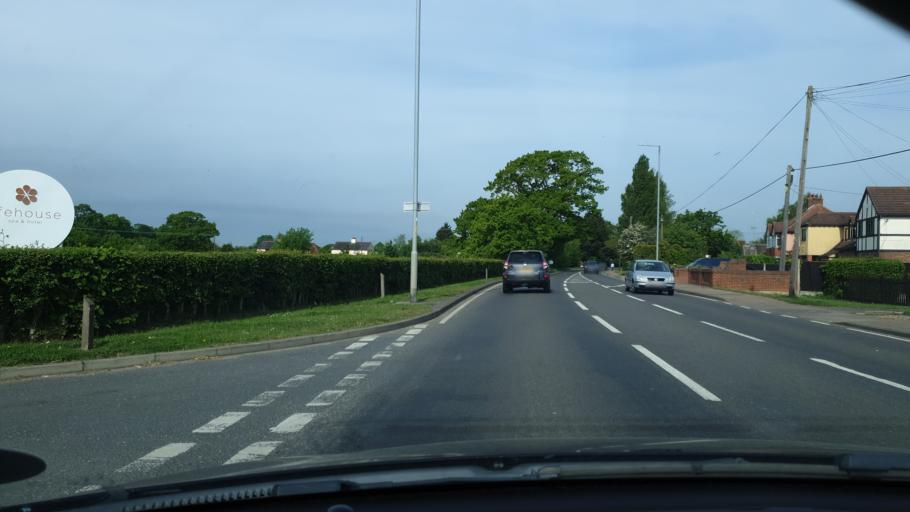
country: GB
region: England
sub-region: Essex
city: Little Clacton
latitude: 51.8543
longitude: 1.1743
